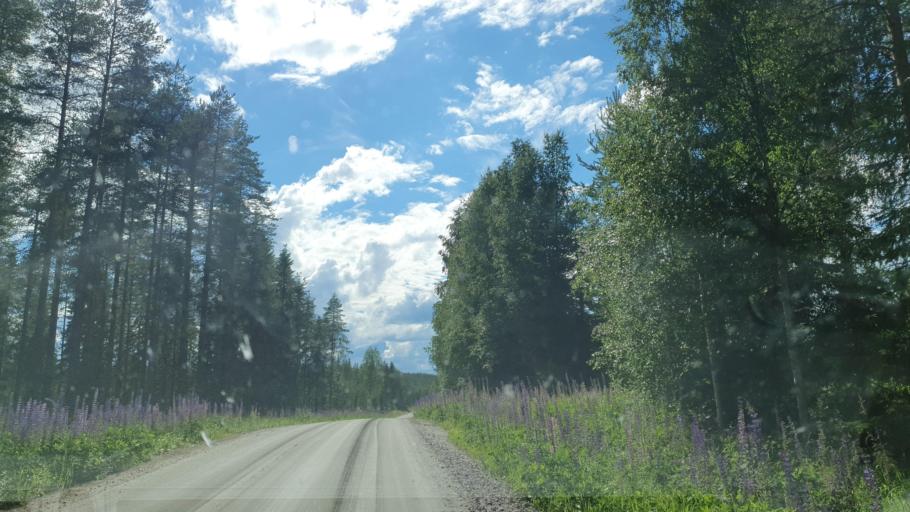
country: FI
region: Kainuu
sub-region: Kehys-Kainuu
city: Kuhmo
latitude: 64.1335
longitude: 29.6643
